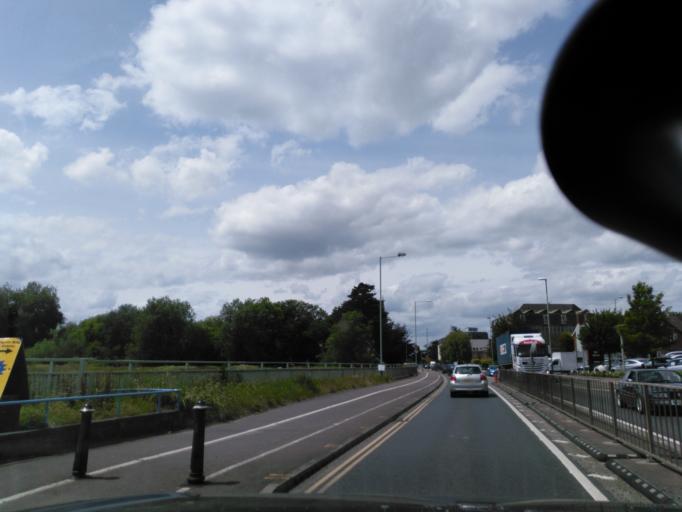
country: GB
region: England
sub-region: Wiltshire
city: Salisbury
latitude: 51.0636
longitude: -1.7837
